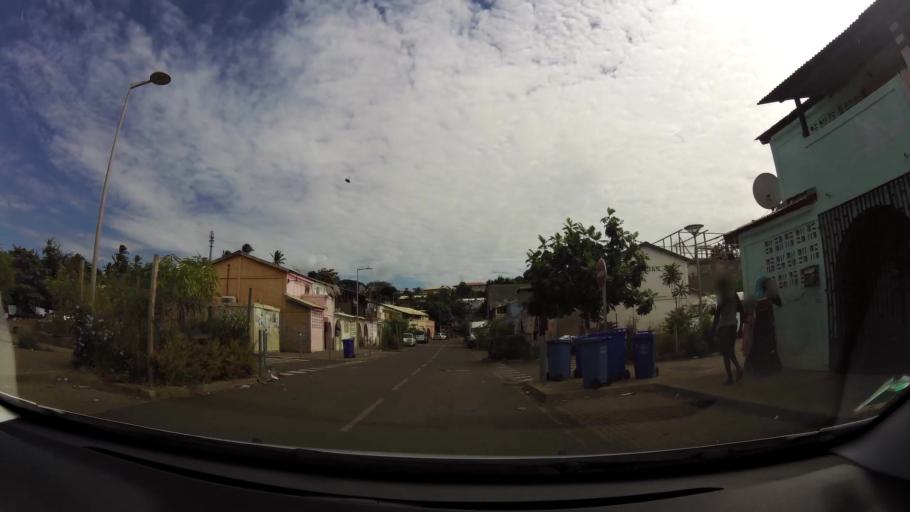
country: YT
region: Mamoudzou
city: Mamoudzou
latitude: -12.7834
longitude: 45.2310
